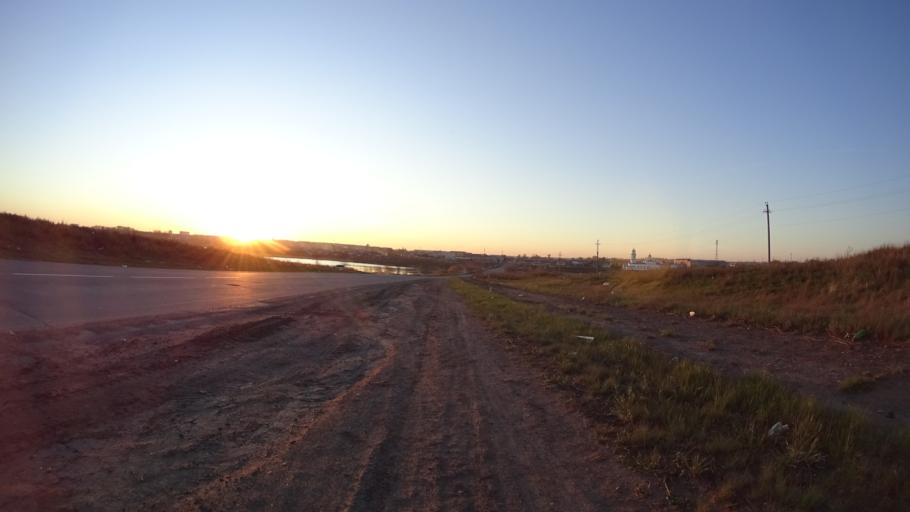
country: RU
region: Chelyabinsk
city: Troitsk
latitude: 54.0721
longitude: 61.5594
